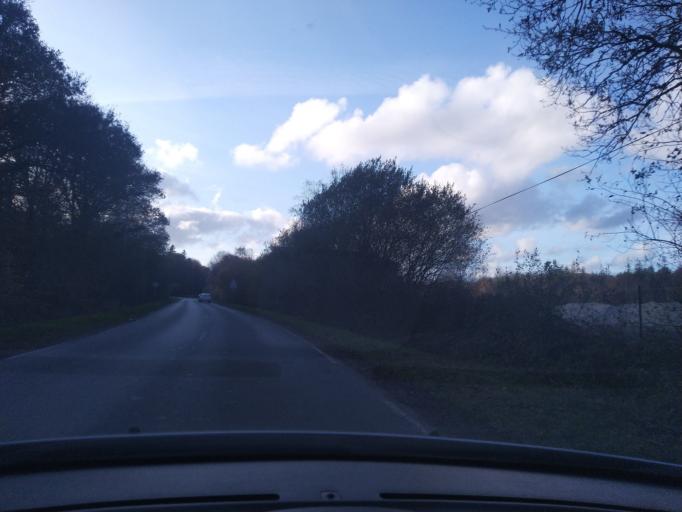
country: FR
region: Brittany
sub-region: Departement du Finistere
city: Morlaix
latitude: 48.5871
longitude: -3.7955
